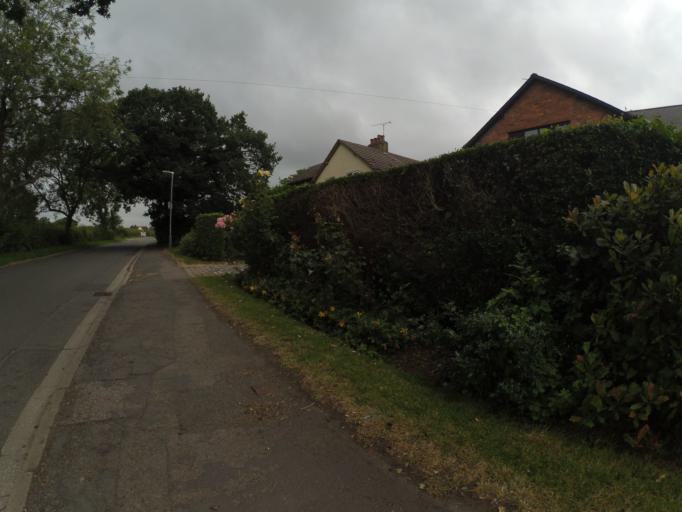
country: GB
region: England
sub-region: Warwickshire
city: Dunchurch
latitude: 52.3431
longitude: -1.2928
